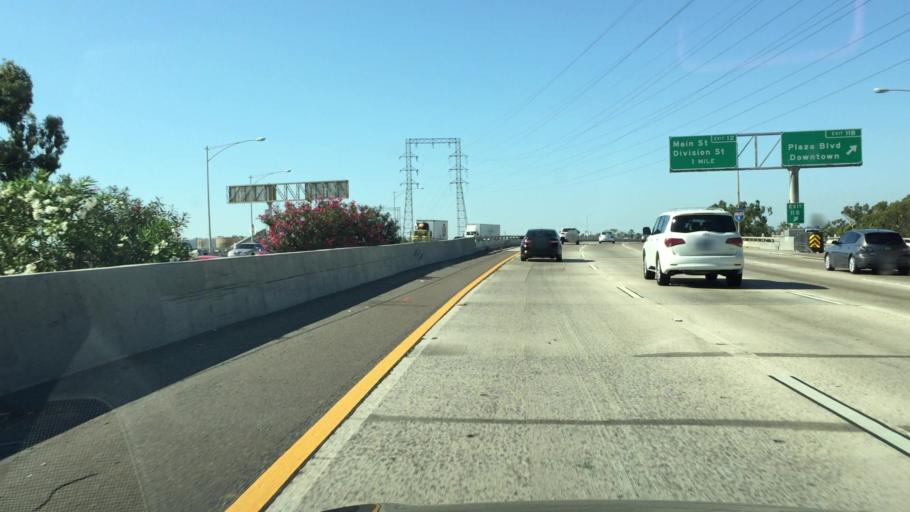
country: US
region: California
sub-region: San Diego County
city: National City
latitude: 32.6691
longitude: -117.1113
